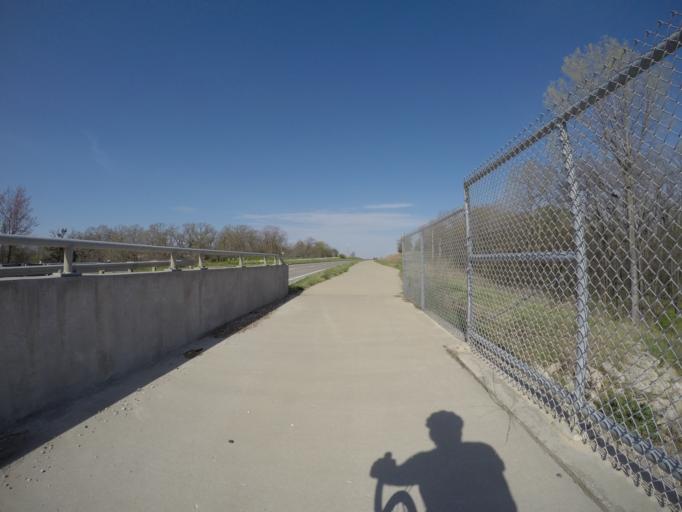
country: US
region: Missouri
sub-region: Cass County
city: Raymore
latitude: 38.8559
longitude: -94.4735
